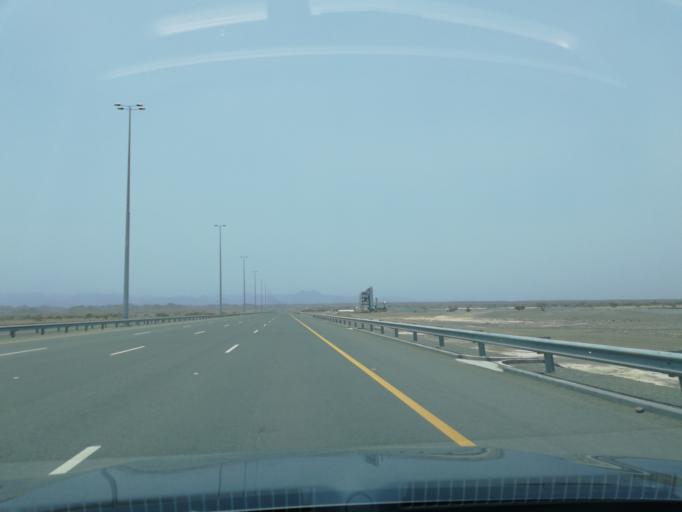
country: OM
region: Al Batinah
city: Al Liwa'
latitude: 24.5459
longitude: 56.4892
